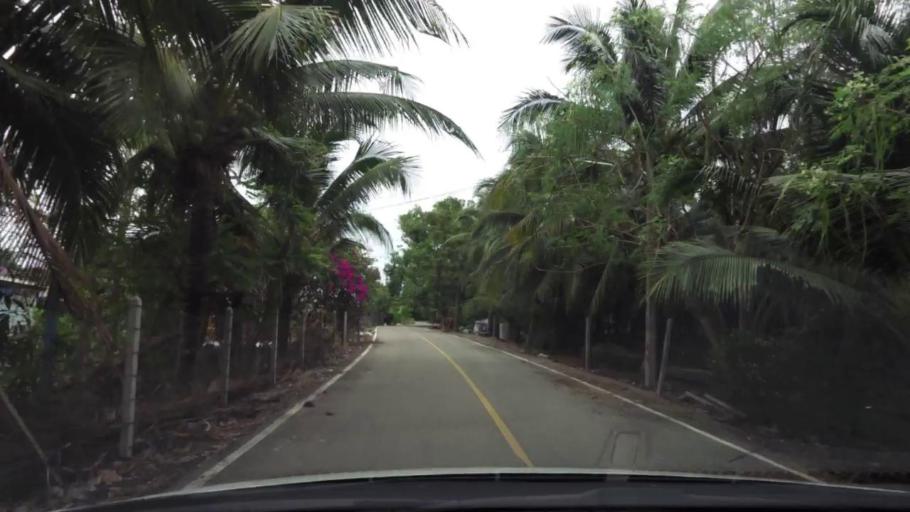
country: TH
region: Samut Sakhon
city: Ban Phaeo
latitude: 13.6064
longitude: 100.0275
